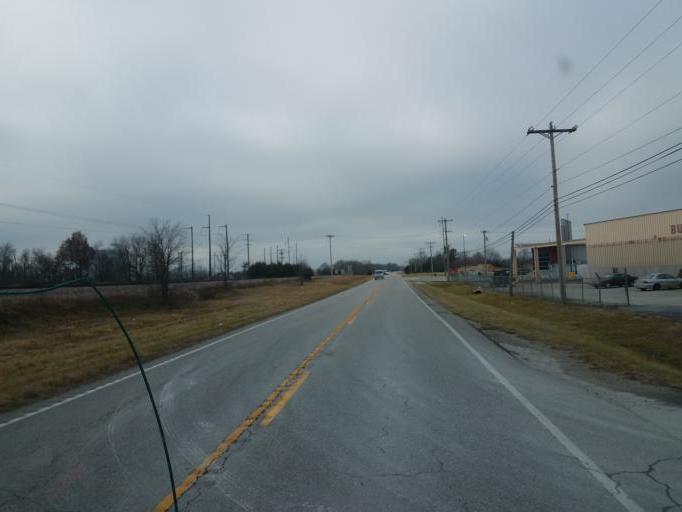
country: US
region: Missouri
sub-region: Greene County
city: Strafford
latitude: 37.2512
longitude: -93.1682
